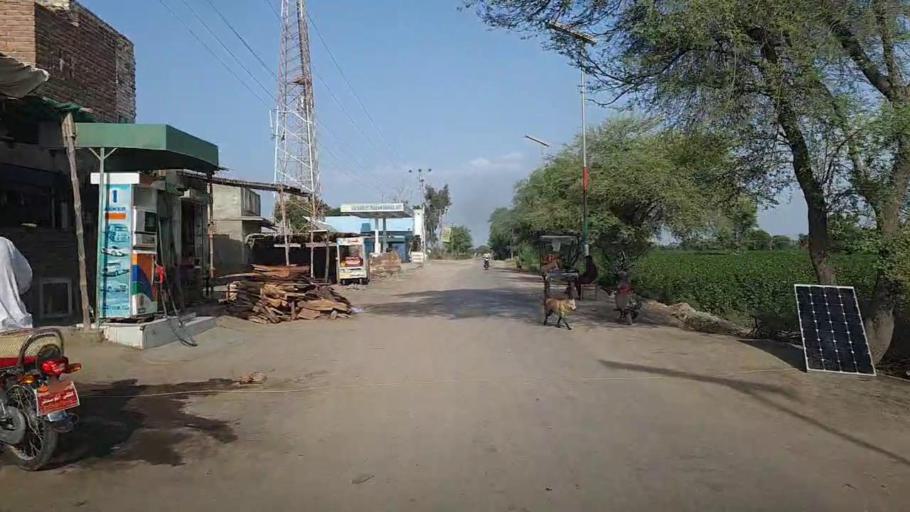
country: PK
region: Sindh
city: Khairpur
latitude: 28.0768
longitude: 69.7972
